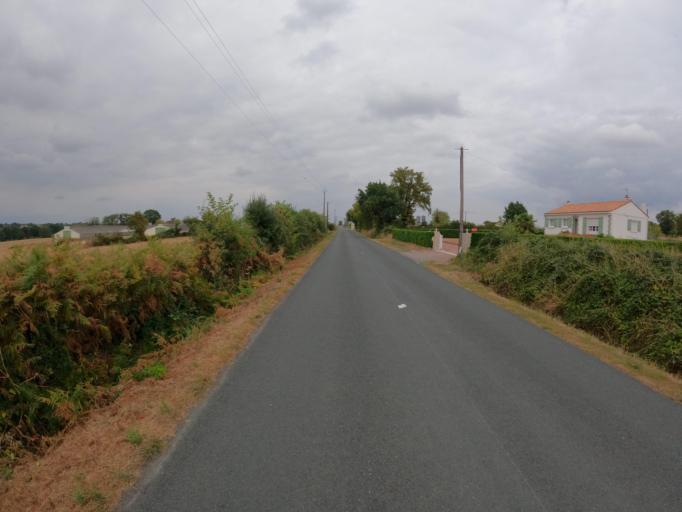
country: FR
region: Pays de la Loire
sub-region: Departement de la Vendee
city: Les Landes-Genusson
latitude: 46.9806
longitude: -1.1123
